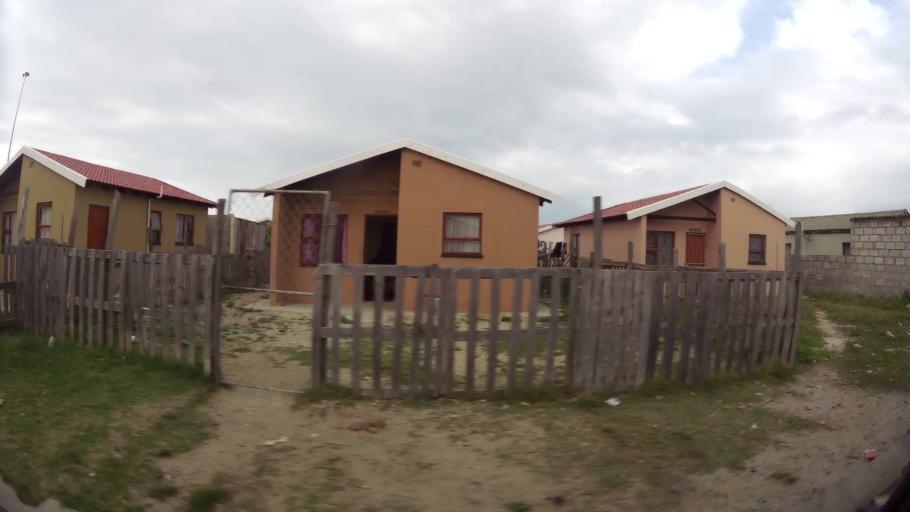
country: ZA
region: Eastern Cape
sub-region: Nelson Mandela Bay Metropolitan Municipality
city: Port Elizabeth
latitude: -33.8946
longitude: 25.6067
